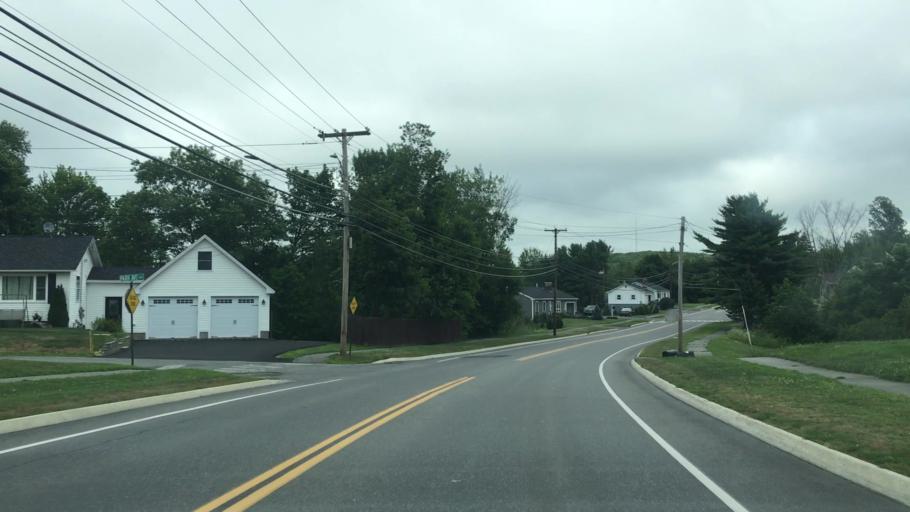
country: US
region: Maine
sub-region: Penobscot County
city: Brewer
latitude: 44.7783
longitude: -68.7675
